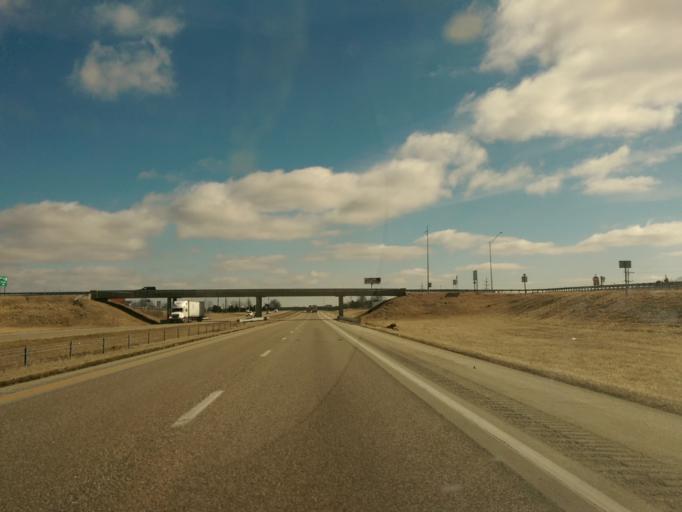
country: US
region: Missouri
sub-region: Montgomery County
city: Montgomery City
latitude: 38.8742
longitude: -91.3748
